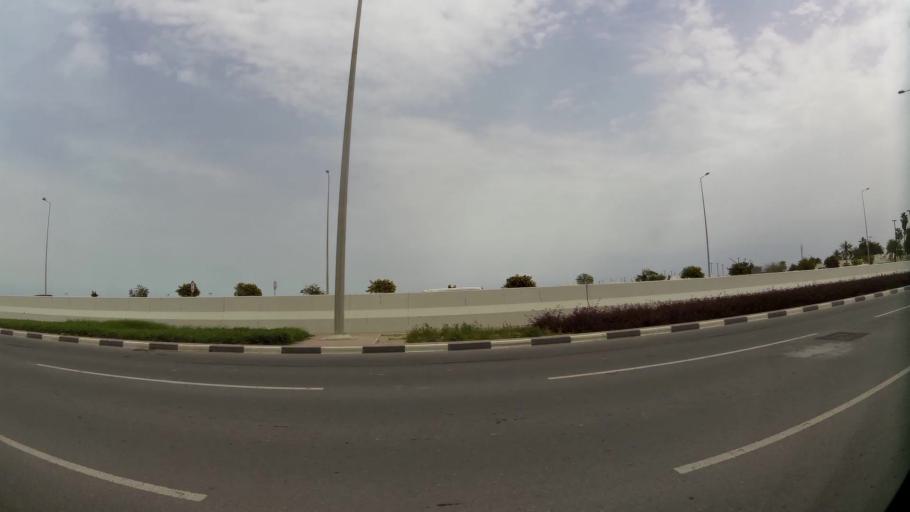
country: QA
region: Baladiyat ad Dawhah
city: Doha
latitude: 25.2861
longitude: 51.5513
